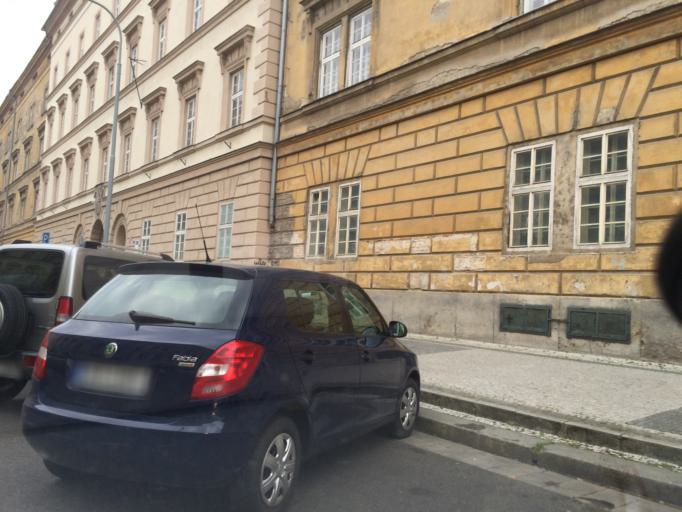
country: CZ
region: Praha
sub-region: Praha 8
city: Karlin
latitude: 50.0908
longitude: 14.4435
